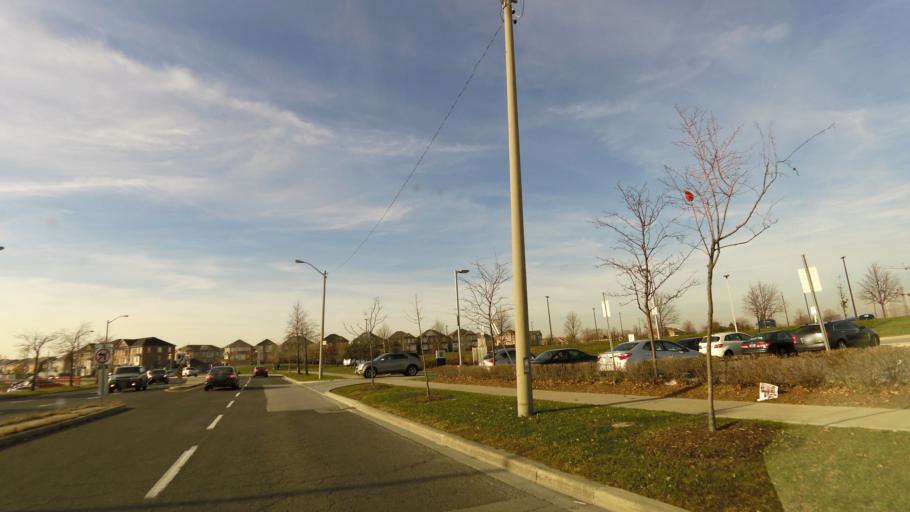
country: CA
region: Ontario
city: Etobicoke
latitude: 43.7228
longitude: -79.5992
